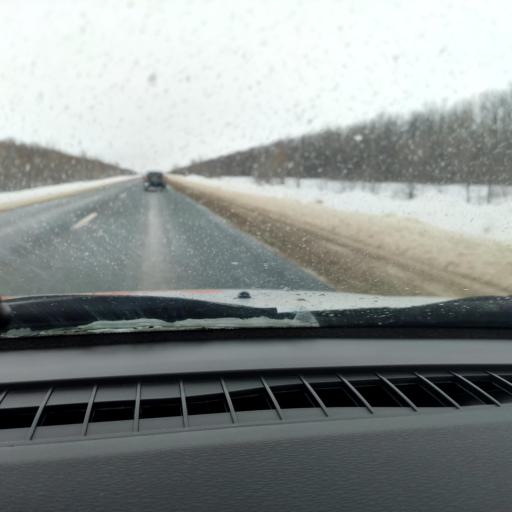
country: RU
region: Samara
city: Mayskoye
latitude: 52.4823
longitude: 50.5381
